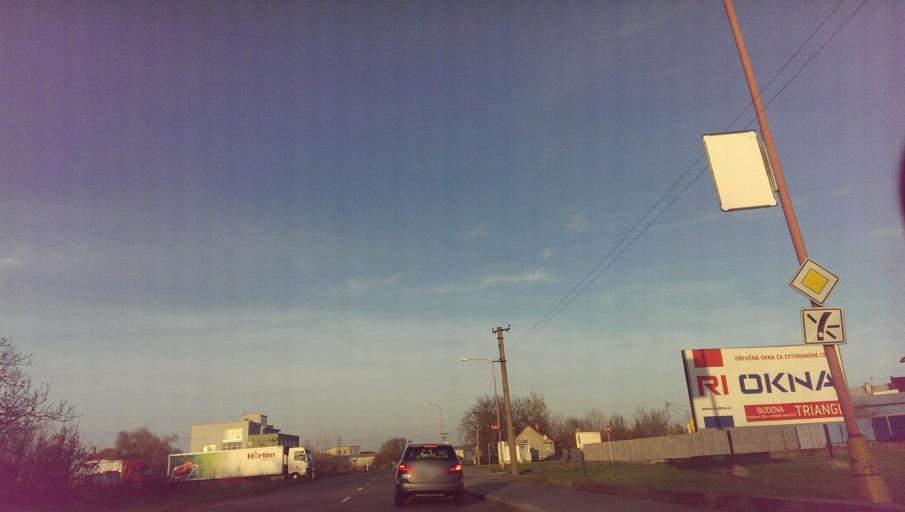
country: CZ
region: Zlin
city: Knezpole
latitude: 49.0883
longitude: 17.4979
